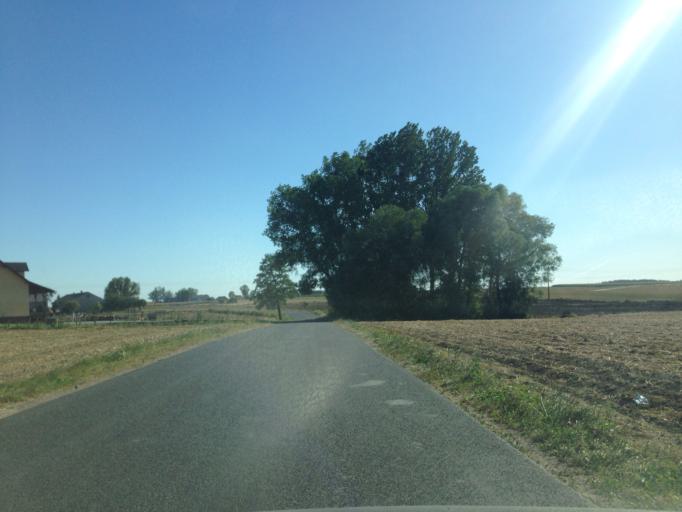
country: PL
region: Kujawsko-Pomorskie
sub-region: Powiat brodnicki
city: Swiedziebnia
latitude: 53.1918
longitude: 19.5630
